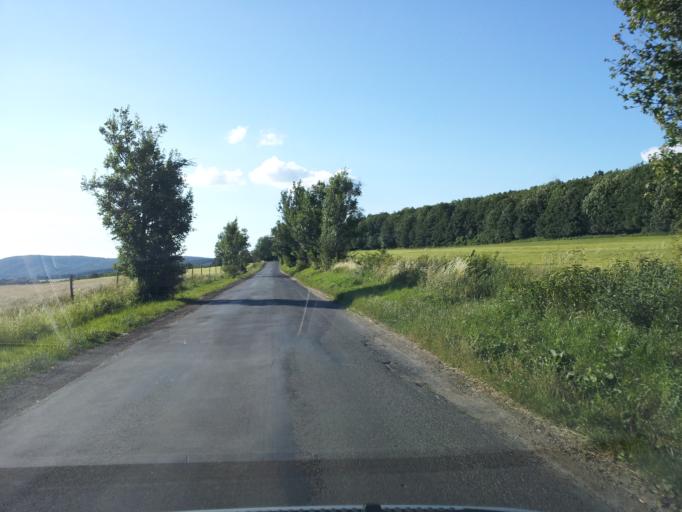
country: HU
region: Veszprem
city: Zirc
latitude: 47.2126
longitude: 17.8430
